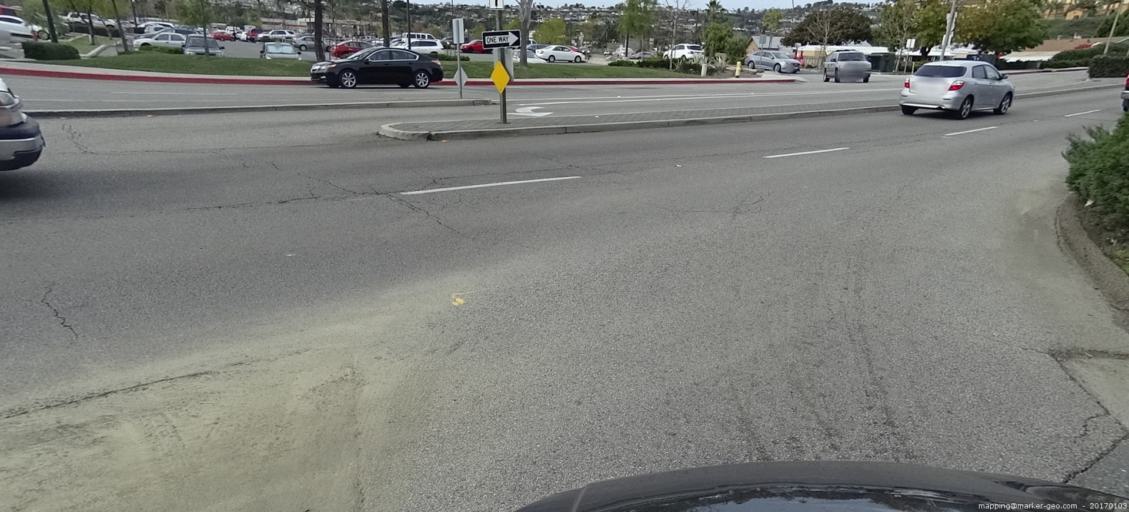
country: US
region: California
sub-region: Orange County
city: Dana Point
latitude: 33.4701
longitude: -117.6755
